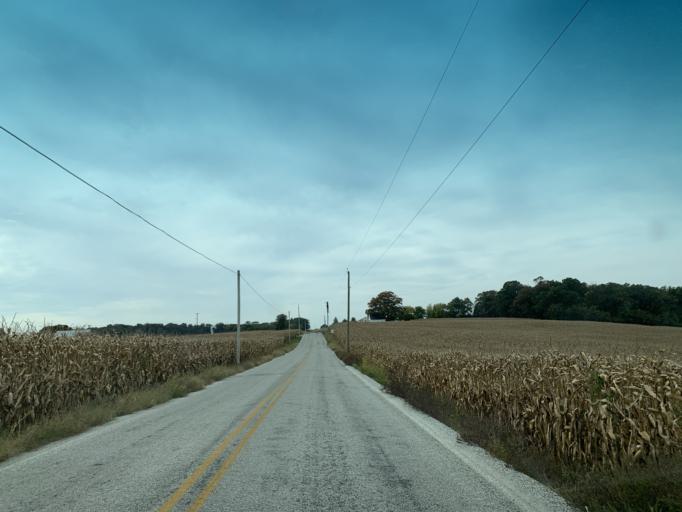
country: US
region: Pennsylvania
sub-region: York County
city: Stewartstown
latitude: 39.8051
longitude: -76.4943
